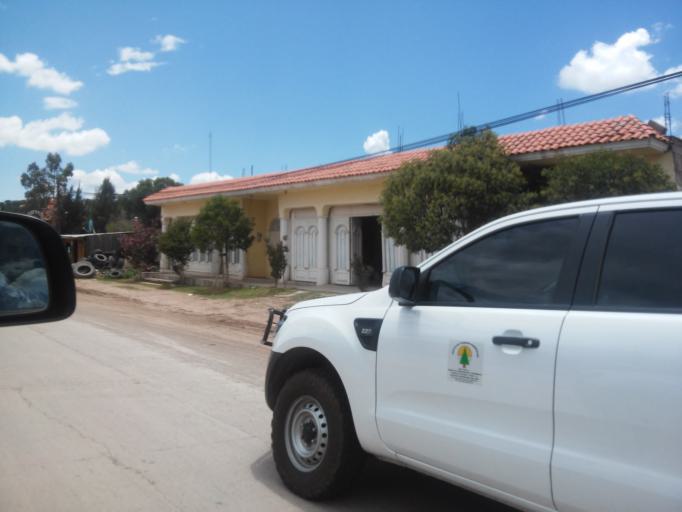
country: MX
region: Durango
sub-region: Santiago Papasquiaro
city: Santiago Papasquiaro
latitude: 25.0647
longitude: -105.4270
